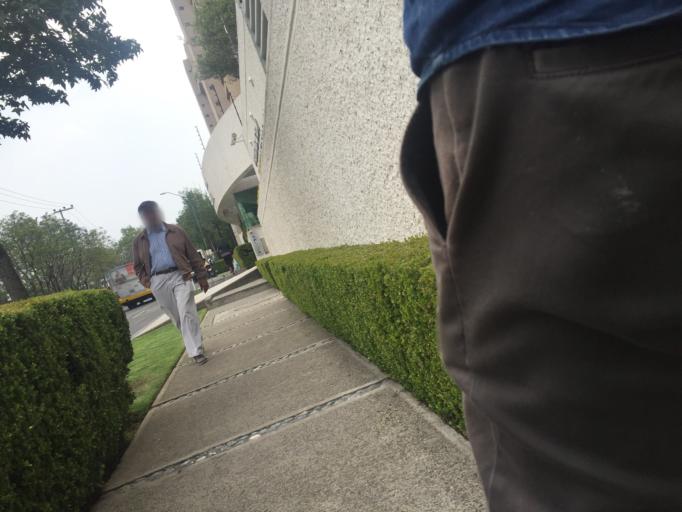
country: MX
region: Mexico City
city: Col. Bosques de las Lomas
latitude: 19.3881
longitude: -99.2630
